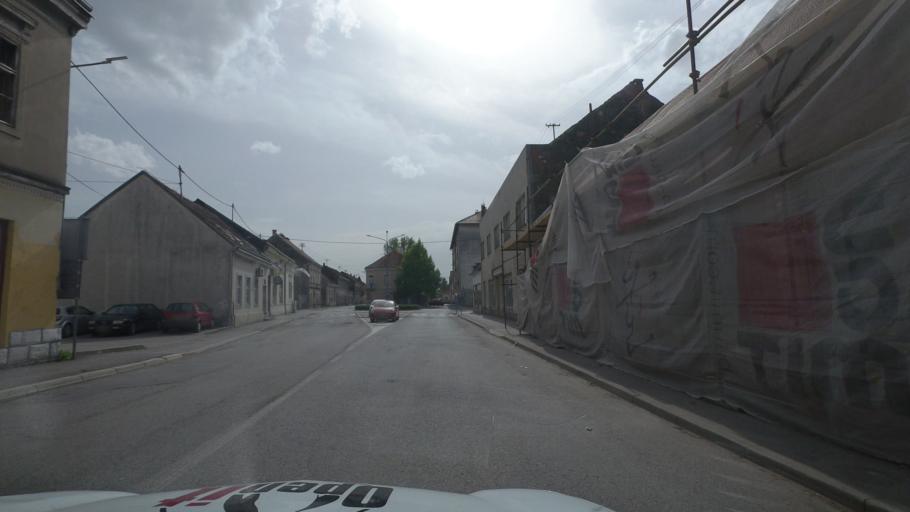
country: HR
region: Sisacko-Moslavacka
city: Glina
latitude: 45.3387
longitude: 16.0914
